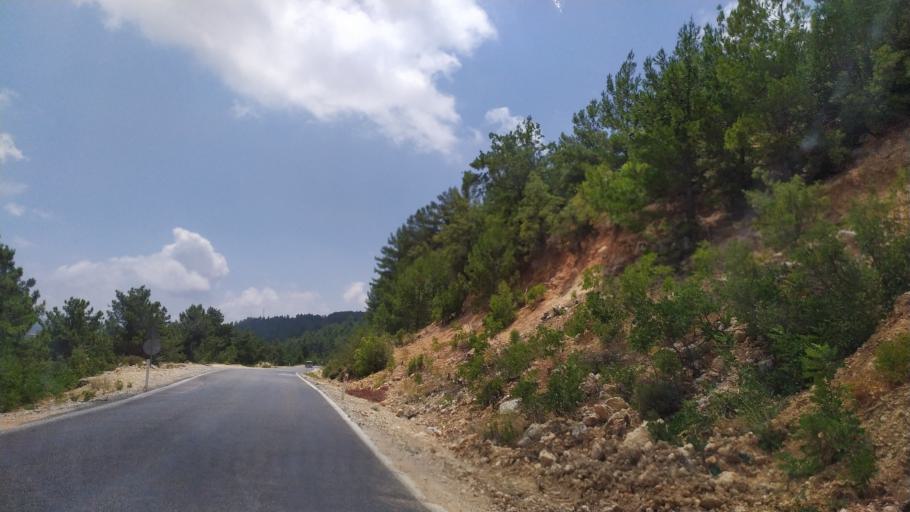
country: TR
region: Mersin
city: Gulnar
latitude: 36.3013
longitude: 33.3806
